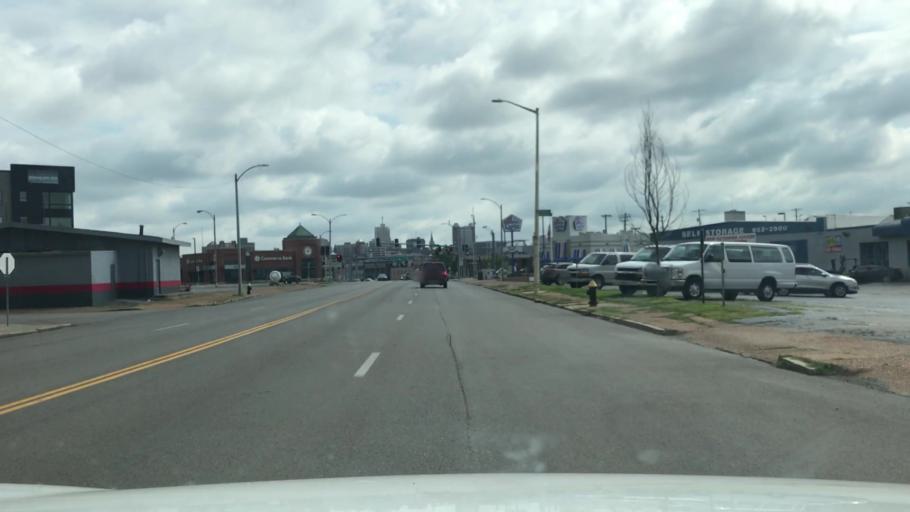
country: US
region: Missouri
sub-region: City of Saint Louis
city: St. Louis
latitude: 38.6274
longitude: -90.2489
